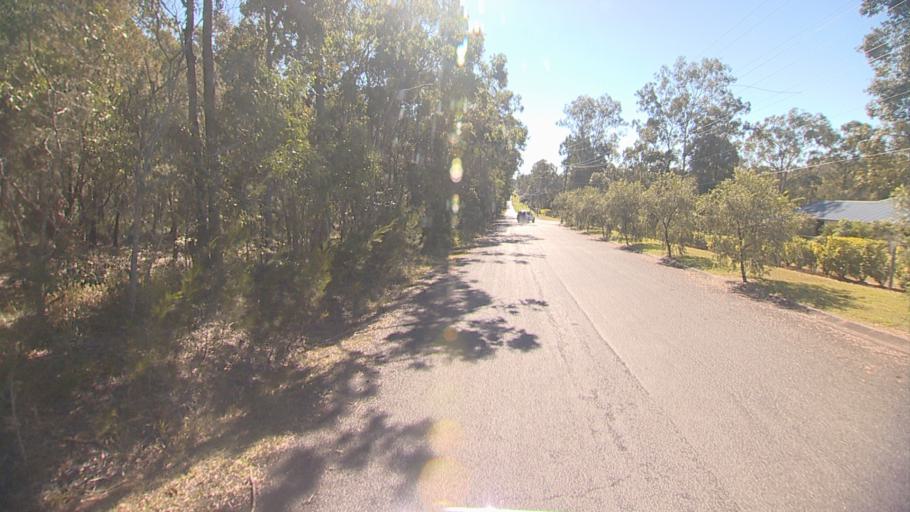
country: AU
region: Queensland
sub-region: Logan
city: Park Ridge South
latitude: -27.6993
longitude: 153.0039
